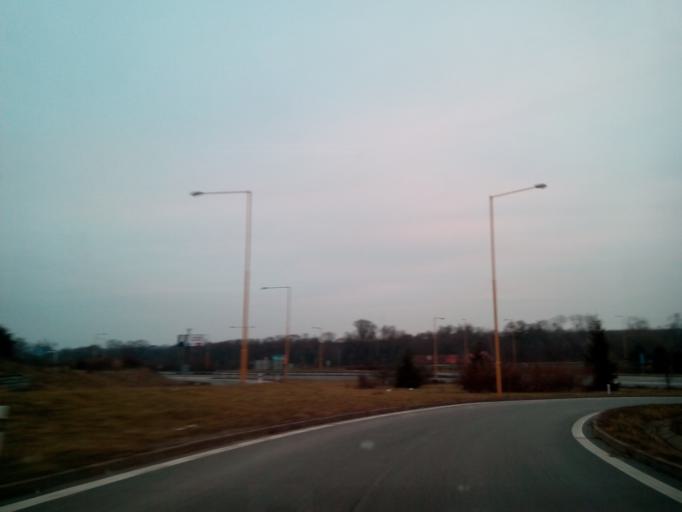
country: SK
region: Kosicky
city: Kosice
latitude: 48.6946
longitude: 21.2350
